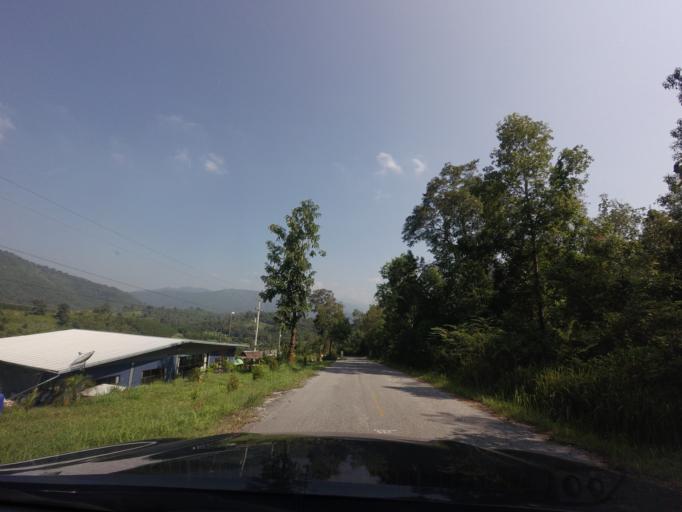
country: TH
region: Loei
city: Na Haeo
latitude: 17.5346
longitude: 101.0033
